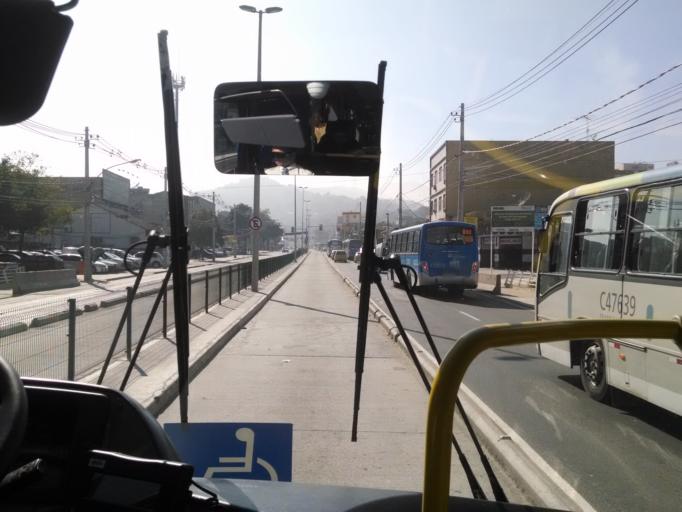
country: BR
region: Rio de Janeiro
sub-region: Sao Joao De Meriti
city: Sao Joao de Meriti
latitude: -22.9194
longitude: -43.3668
